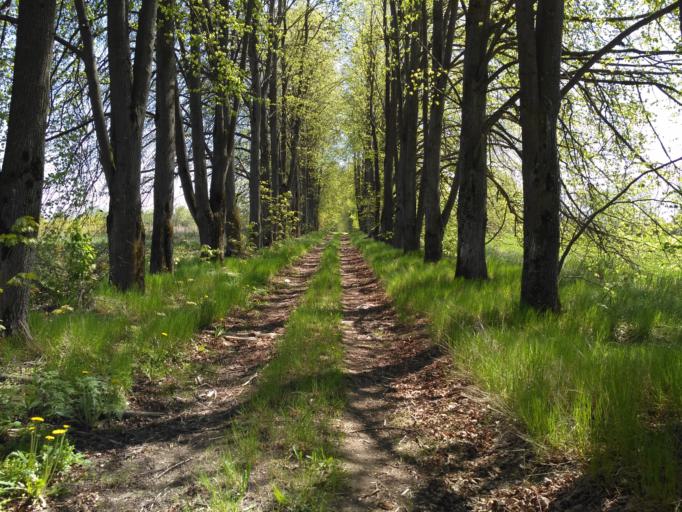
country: BY
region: Minsk
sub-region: Smalyavitski Rayon
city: Oktjabr'skij
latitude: 53.9680
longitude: 28.2762
